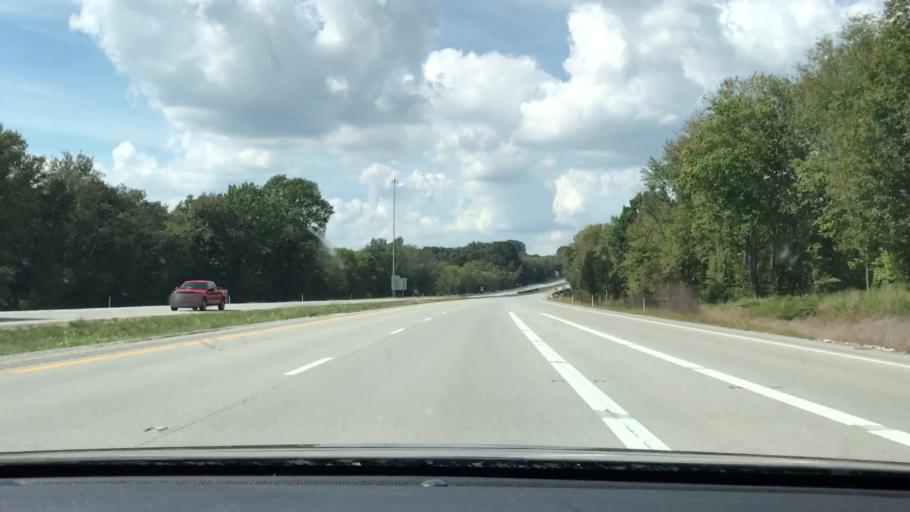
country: US
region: Kentucky
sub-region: Barren County
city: Glasgow
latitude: 36.9936
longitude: -85.9843
